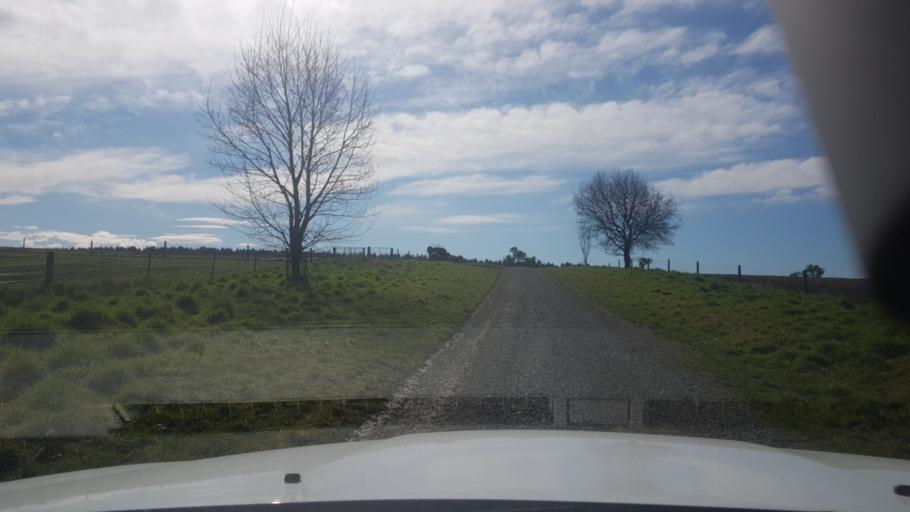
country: NZ
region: Canterbury
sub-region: Timaru District
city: Pleasant Point
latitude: -44.1990
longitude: 171.1874
